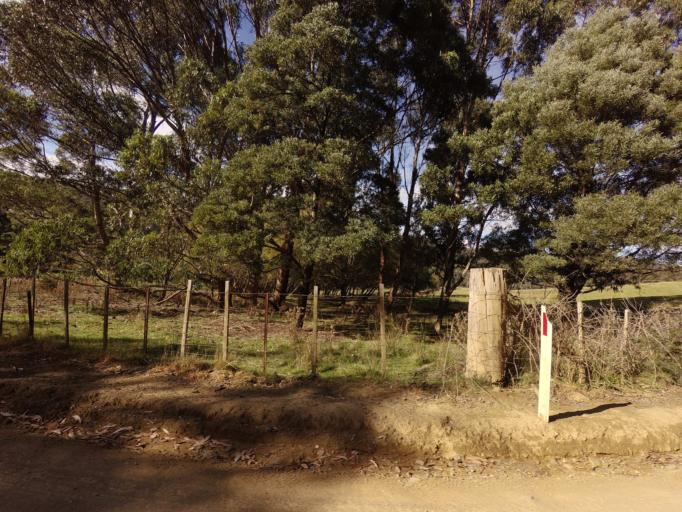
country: AU
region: Tasmania
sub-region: Clarence
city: Sandford
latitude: -43.1357
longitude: 147.7660
